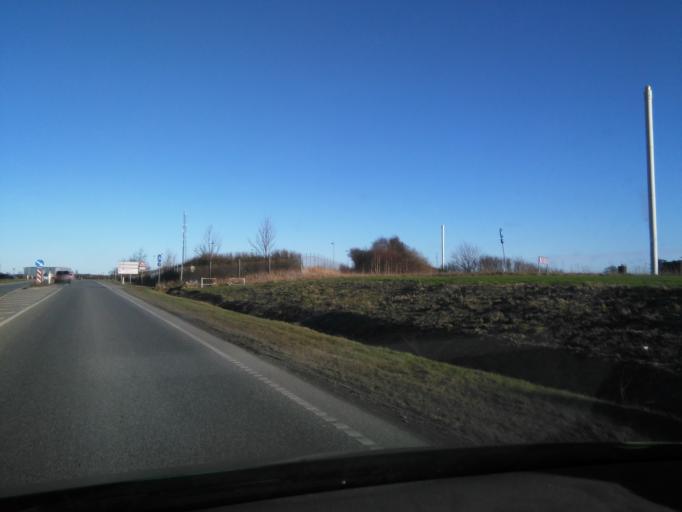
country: DK
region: North Denmark
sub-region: Mariagerfjord Kommune
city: Hobro
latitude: 56.6558
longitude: 9.7989
